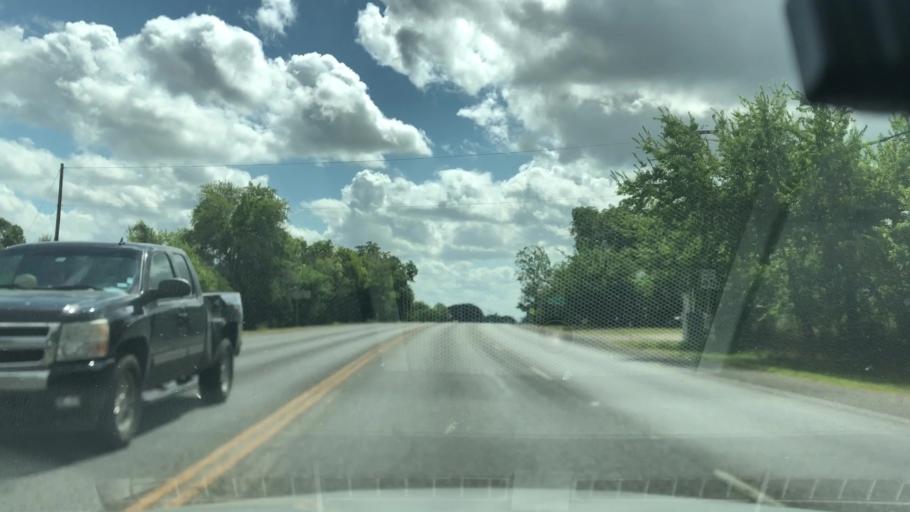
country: US
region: Texas
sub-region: Guadalupe County
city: Seguin
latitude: 29.5692
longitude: -97.9986
